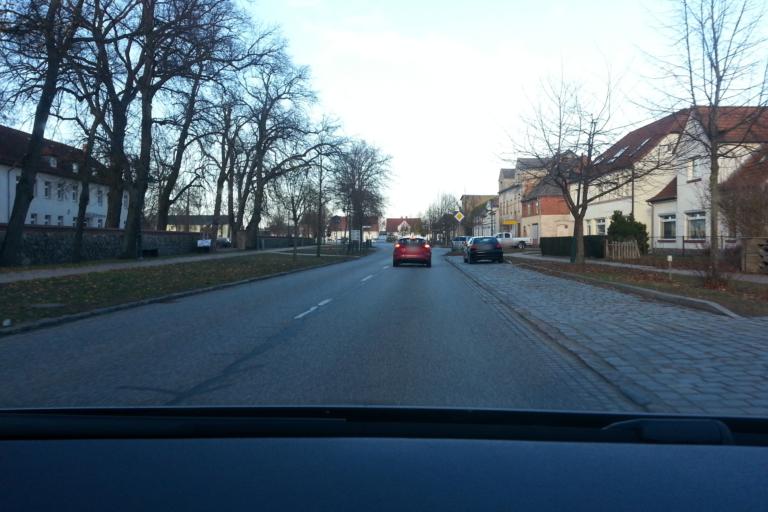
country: DE
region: Mecklenburg-Vorpommern
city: Ferdinandshof
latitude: 53.6641
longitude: 13.8888
